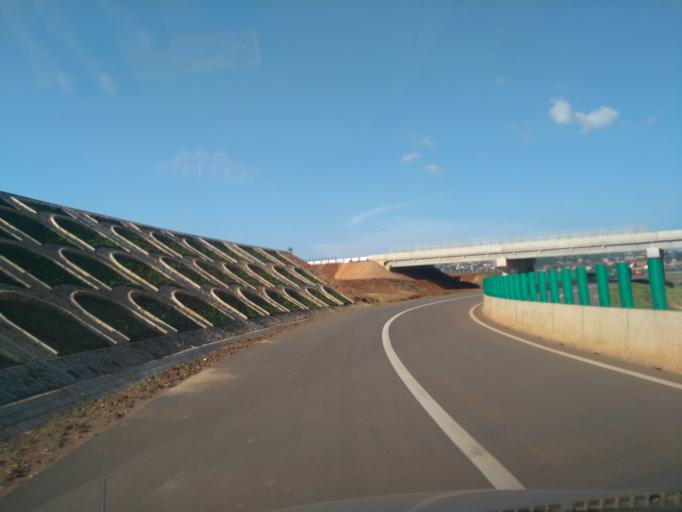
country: UG
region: Central Region
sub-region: Wakiso District
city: Kajansi
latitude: 0.2152
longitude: 32.5301
